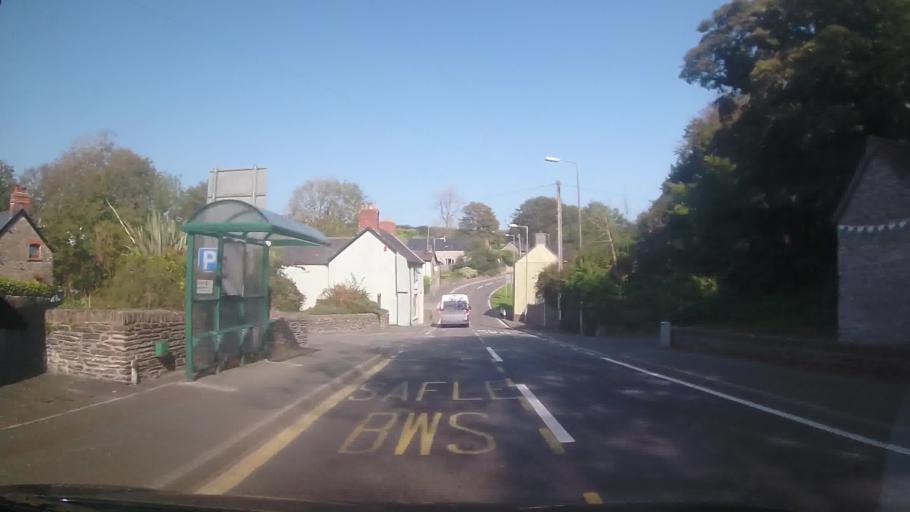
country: GB
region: Wales
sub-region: Pembrokeshire
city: Crymych
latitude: 52.0139
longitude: -4.7091
